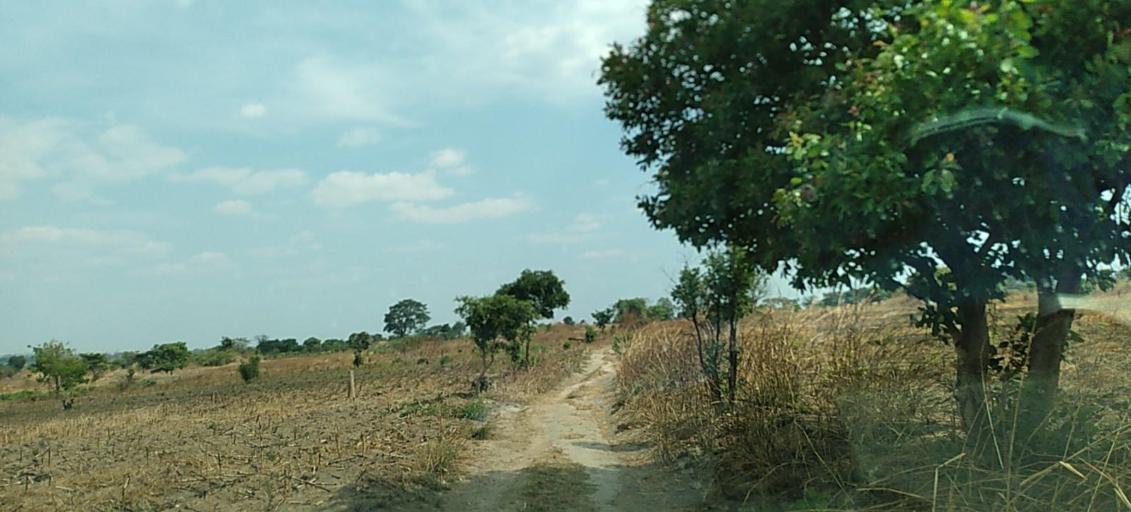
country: ZM
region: Copperbelt
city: Chililabombwe
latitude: -12.3480
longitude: 27.7932
